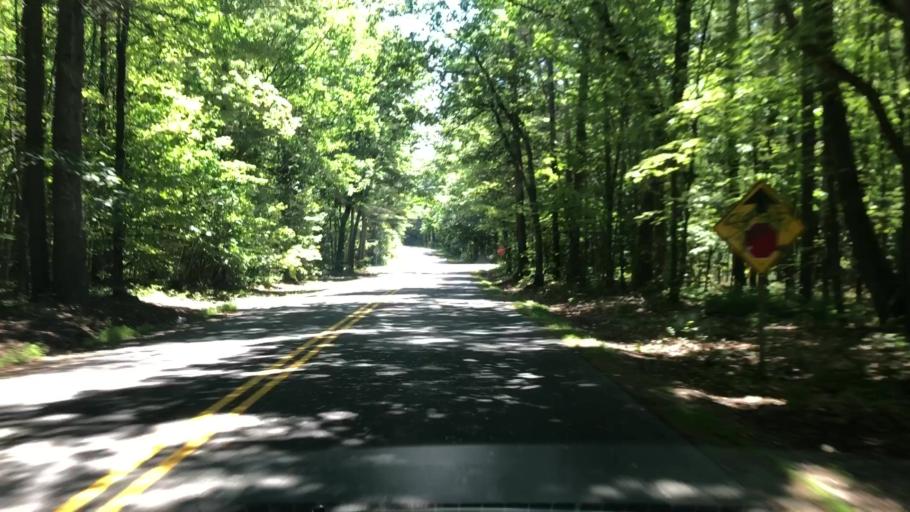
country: US
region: New Hampshire
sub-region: Hillsborough County
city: Milford
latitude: 42.8400
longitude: -71.5717
